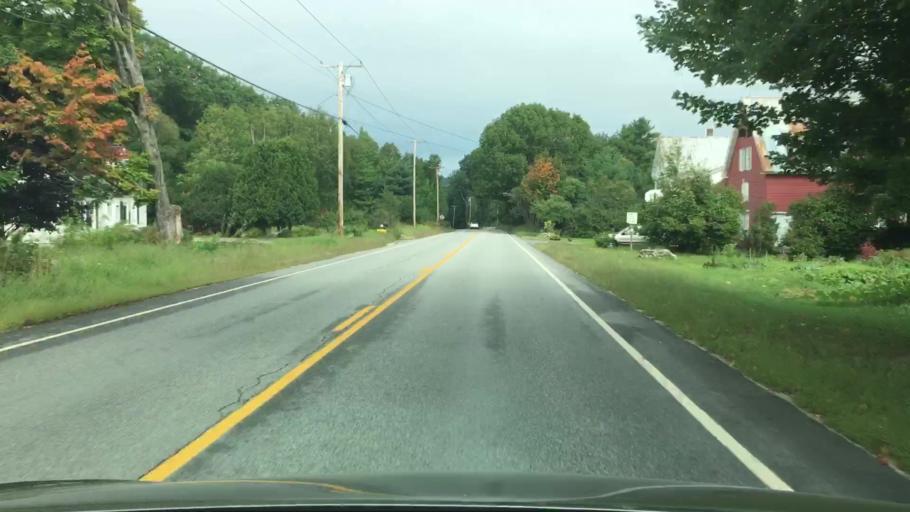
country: US
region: Maine
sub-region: Androscoggin County
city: Livermore
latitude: 44.3366
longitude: -70.2923
